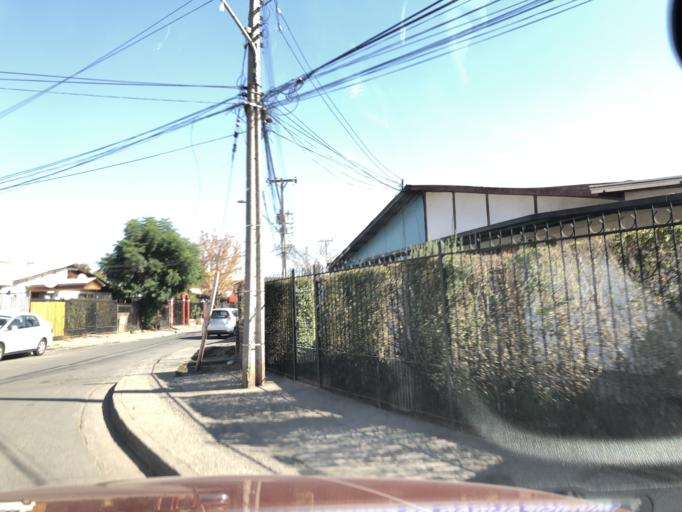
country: CL
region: Santiago Metropolitan
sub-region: Provincia de Cordillera
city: Puente Alto
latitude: -33.5664
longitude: -70.5739
